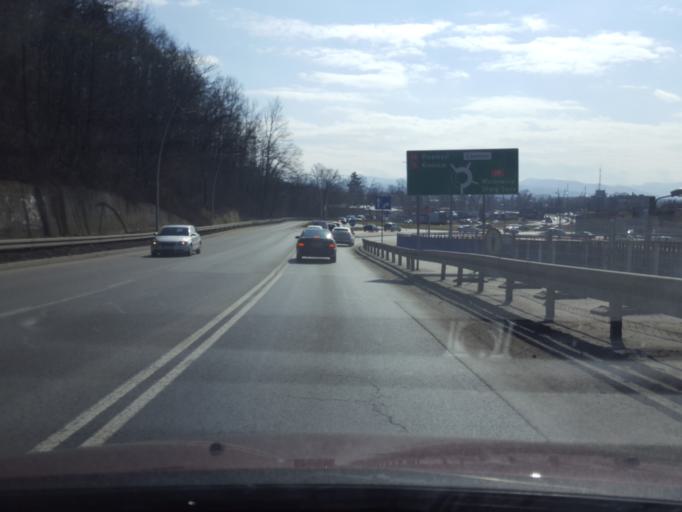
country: PL
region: Lesser Poland Voivodeship
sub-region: Powiat nowosadecki
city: Nowy Sacz
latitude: 49.6416
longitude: 20.6922
